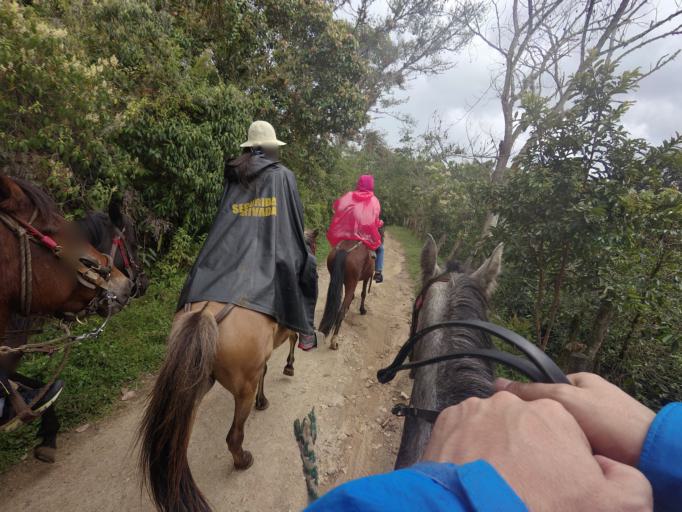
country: CO
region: Huila
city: San Agustin
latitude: 1.9027
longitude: -76.2921
